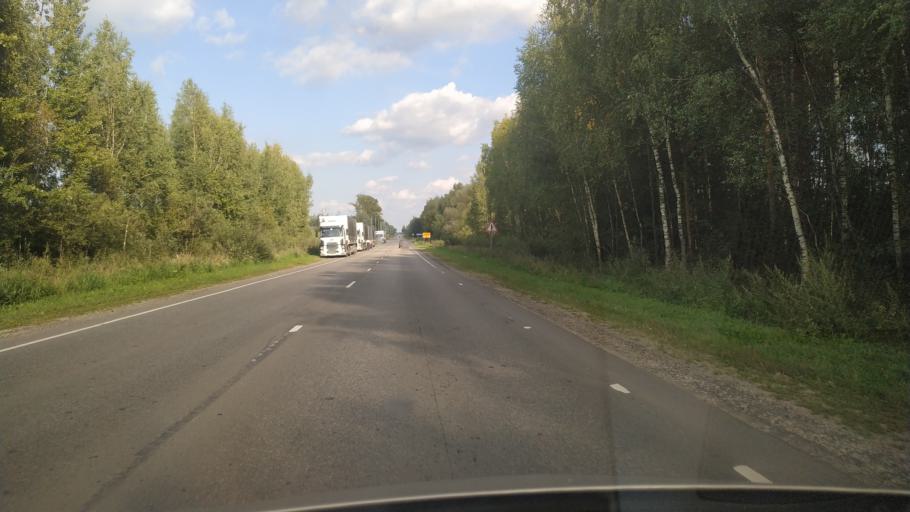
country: RU
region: Moskovskaya
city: Vereya
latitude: 55.7087
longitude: 39.0887
